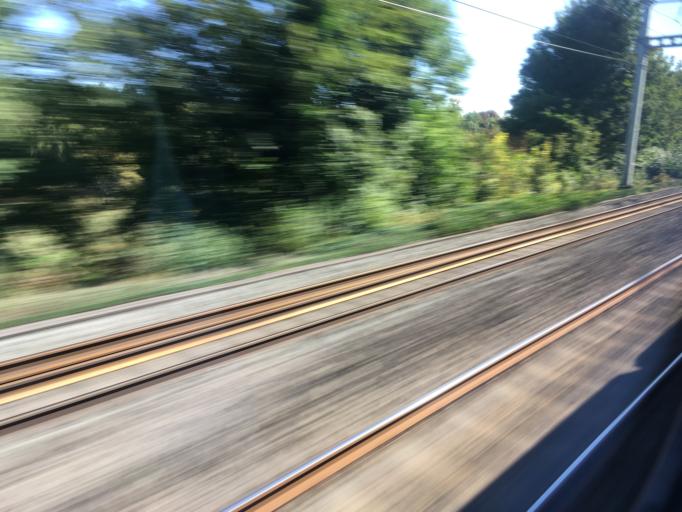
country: GB
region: England
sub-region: West Berkshire
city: Basildon
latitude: 51.4917
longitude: -1.1064
